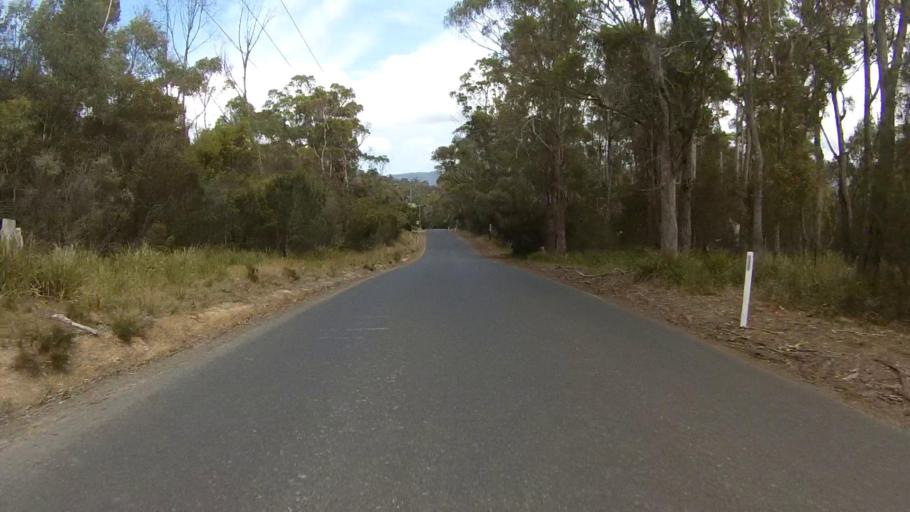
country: AU
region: Tasmania
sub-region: Kingborough
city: Blackmans Bay
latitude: -43.0278
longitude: 147.3127
